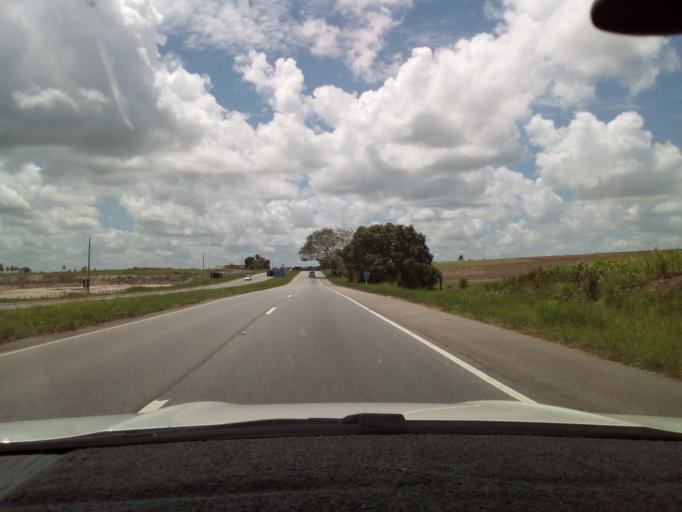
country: BR
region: Paraiba
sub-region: Pilar
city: Pilar
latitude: -7.1889
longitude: -35.2788
